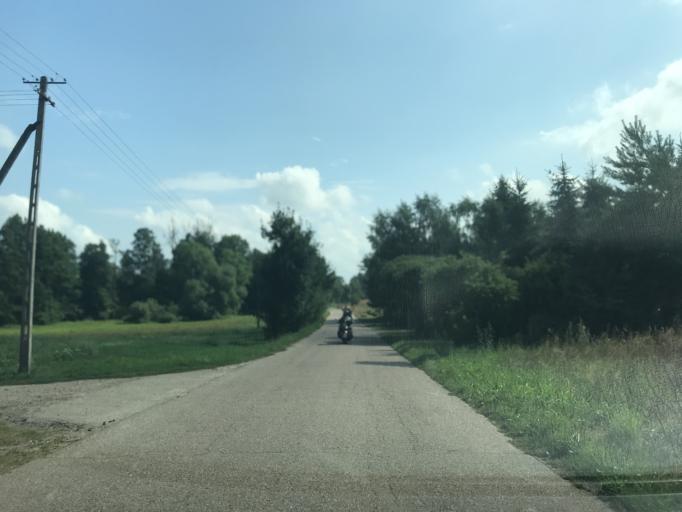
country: PL
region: Warmian-Masurian Voivodeship
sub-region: Powiat nowomiejski
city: Biskupiec
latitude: 53.4473
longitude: 19.4461
